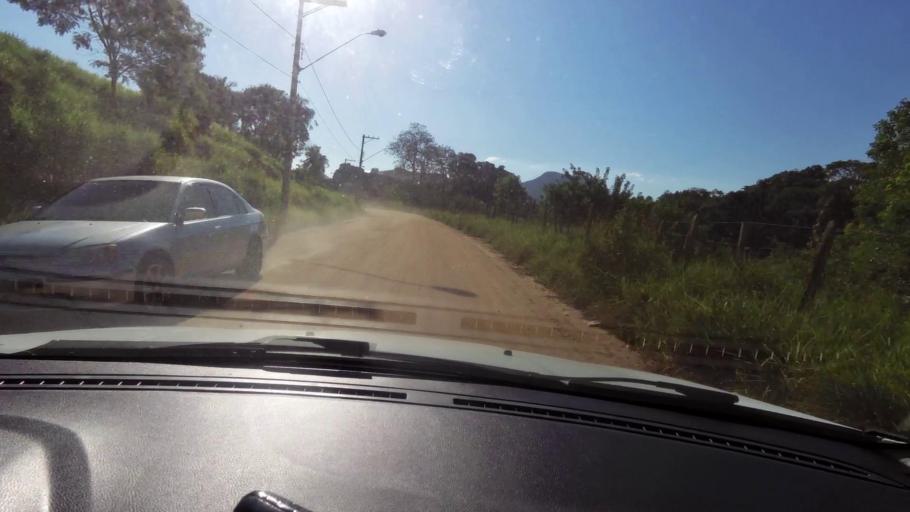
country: BR
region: Espirito Santo
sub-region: Guarapari
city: Guarapari
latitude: -20.6479
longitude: -40.5087
